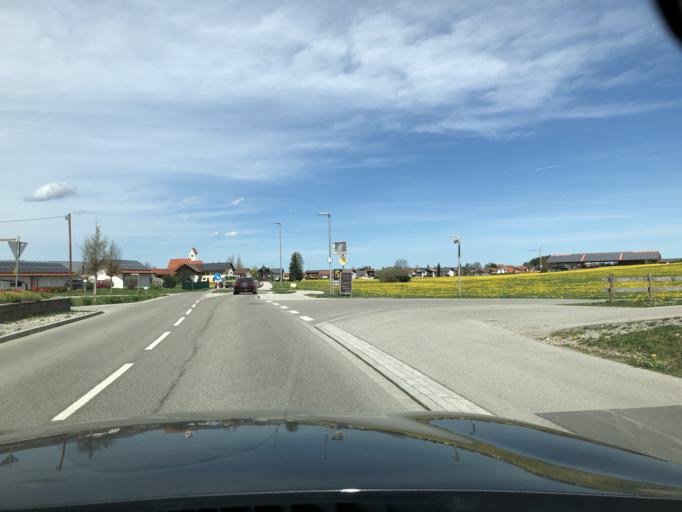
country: DE
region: Bavaria
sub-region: Swabia
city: Lengenwang
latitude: 47.6947
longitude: 10.6070
